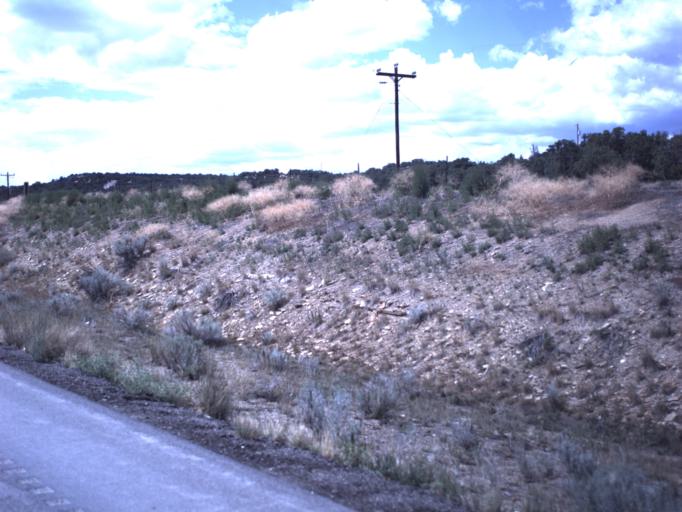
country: US
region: Utah
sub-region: Duchesne County
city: Duchesne
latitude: 40.1713
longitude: -110.5687
